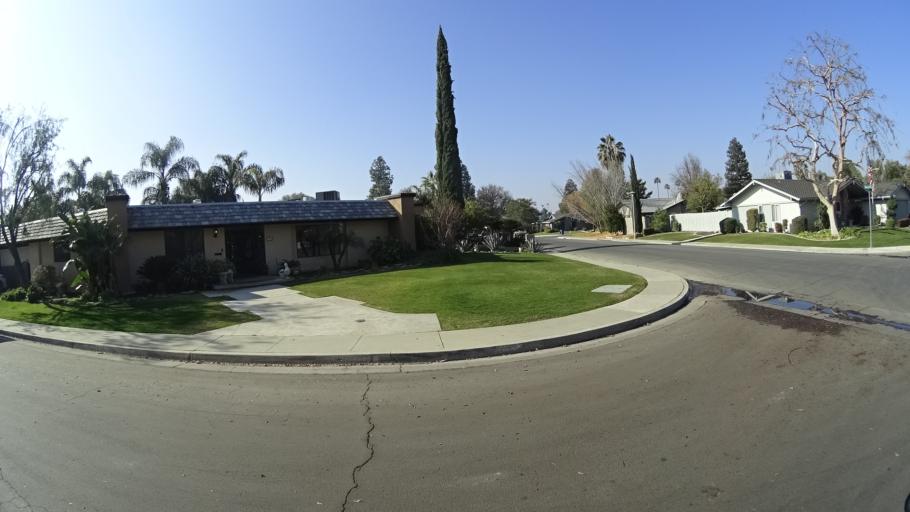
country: US
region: California
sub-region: Kern County
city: Greenacres
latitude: 35.3579
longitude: -119.0730
